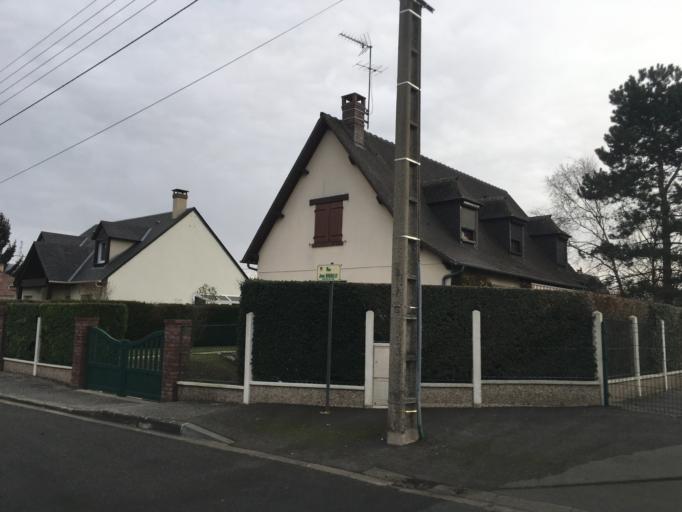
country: FR
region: Haute-Normandie
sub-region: Departement de l'Eure
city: Vernon
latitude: 49.0848
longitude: 1.4903
